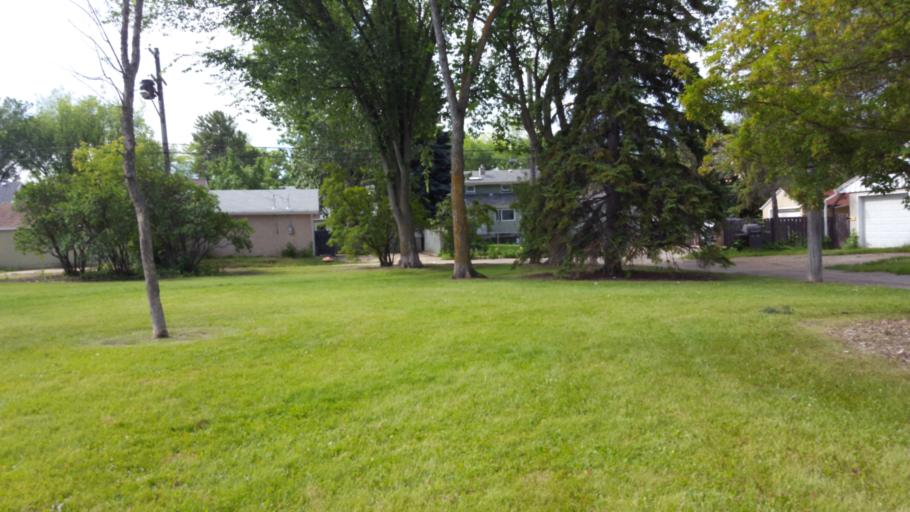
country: CA
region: Alberta
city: Edmonton
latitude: 53.5149
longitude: -113.5310
